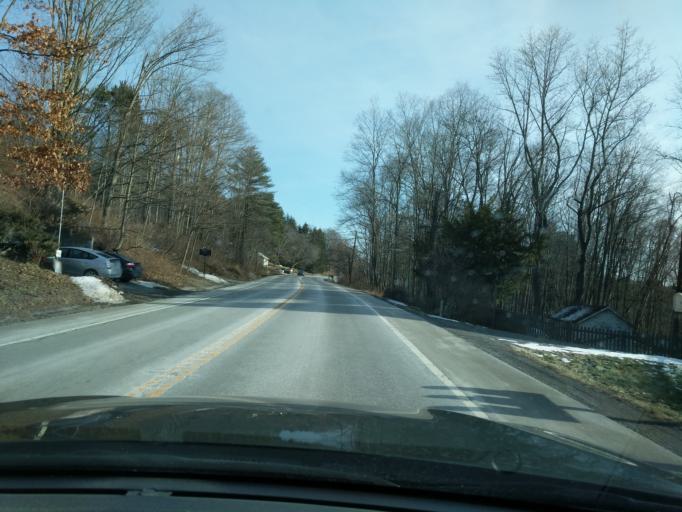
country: US
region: New York
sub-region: Tompkins County
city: East Ithaca
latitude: 42.4108
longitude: -76.4411
